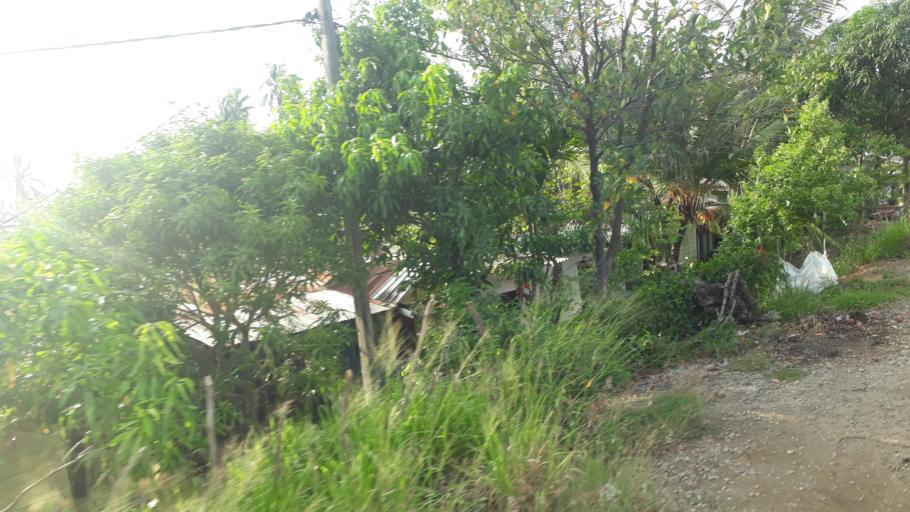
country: LK
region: Western
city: Kolonnawa
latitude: 6.9465
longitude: 79.8862
